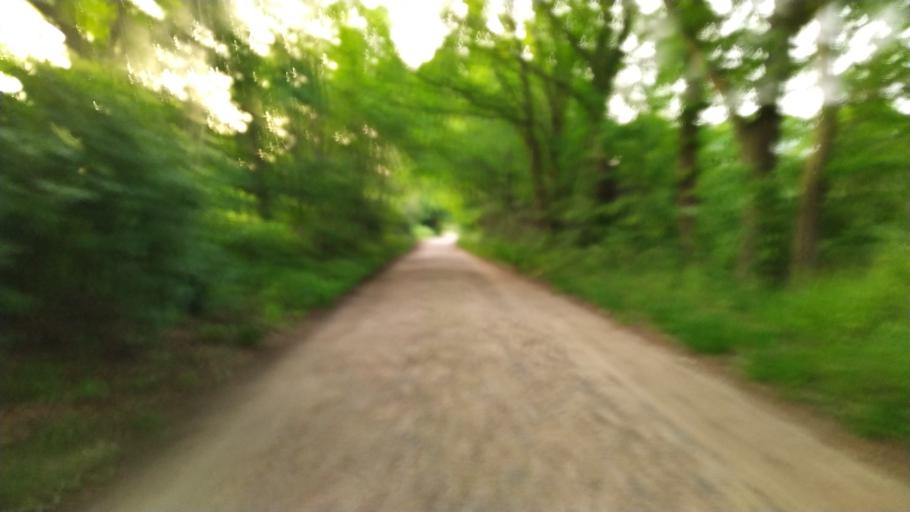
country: DE
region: Lower Saxony
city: Neu Wulmstorf
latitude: 53.4771
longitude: 9.8284
